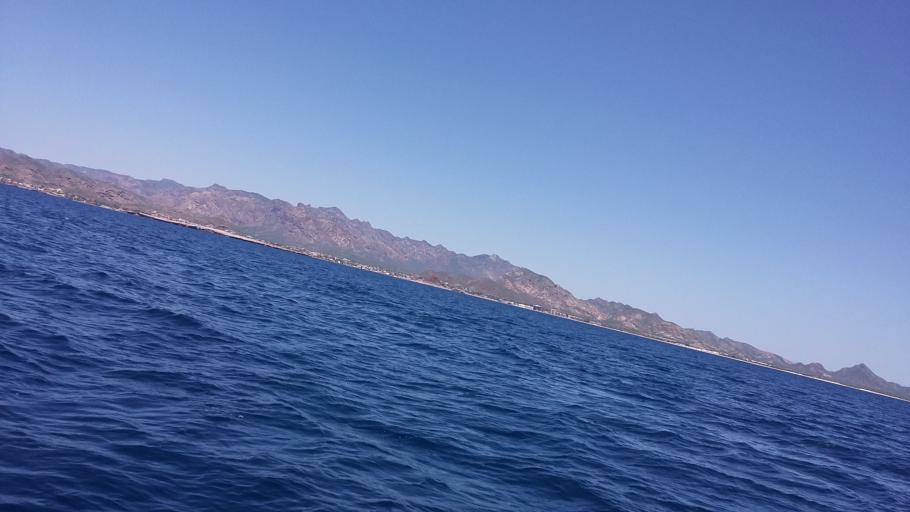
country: MX
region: Sonora
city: Heroica Guaymas
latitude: 27.9281
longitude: -111.0158
